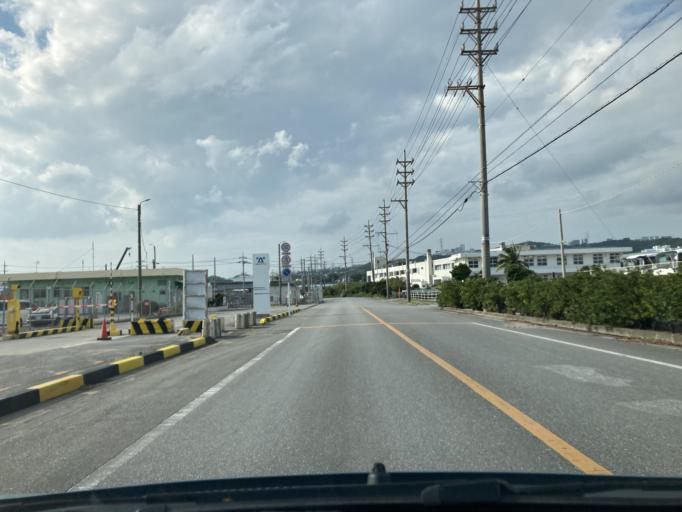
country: JP
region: Okinawa
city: Ginowan
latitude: 26.2269
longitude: 127.7784
